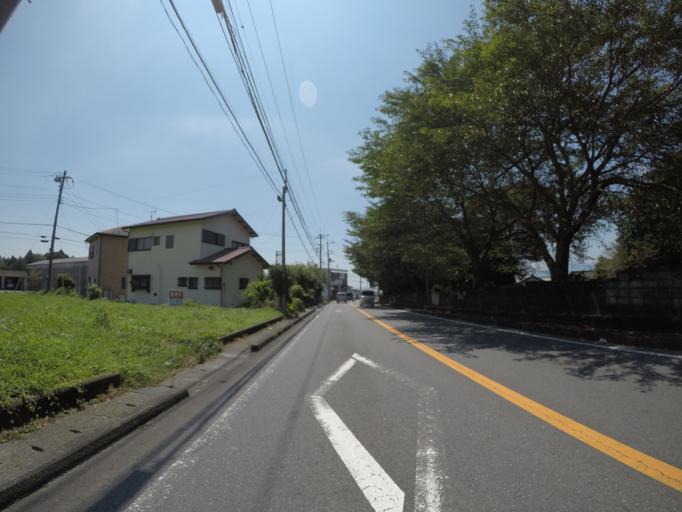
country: JP
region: Shizuoka
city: Fuji
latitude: 35.2033
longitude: 138.6842
